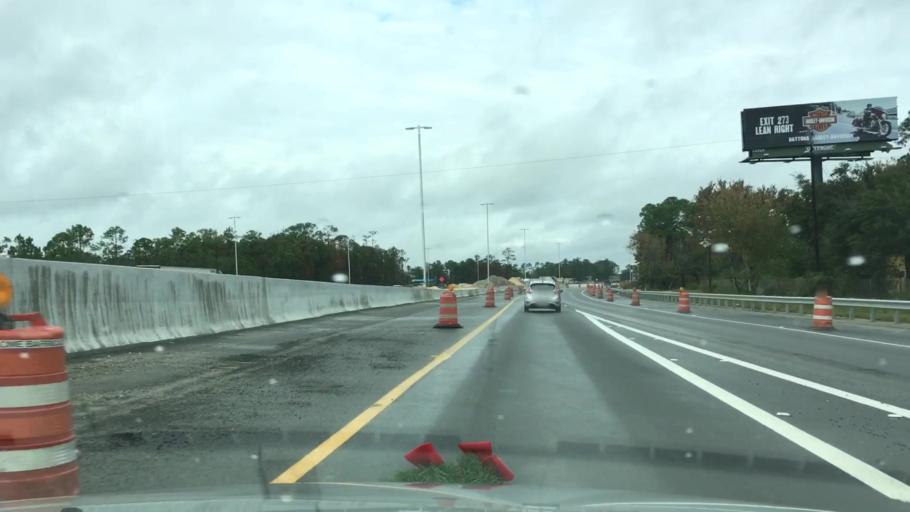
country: US
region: Florida
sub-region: Volusia County
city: Daytona Beach
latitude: 29.1762
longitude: -81.0872
